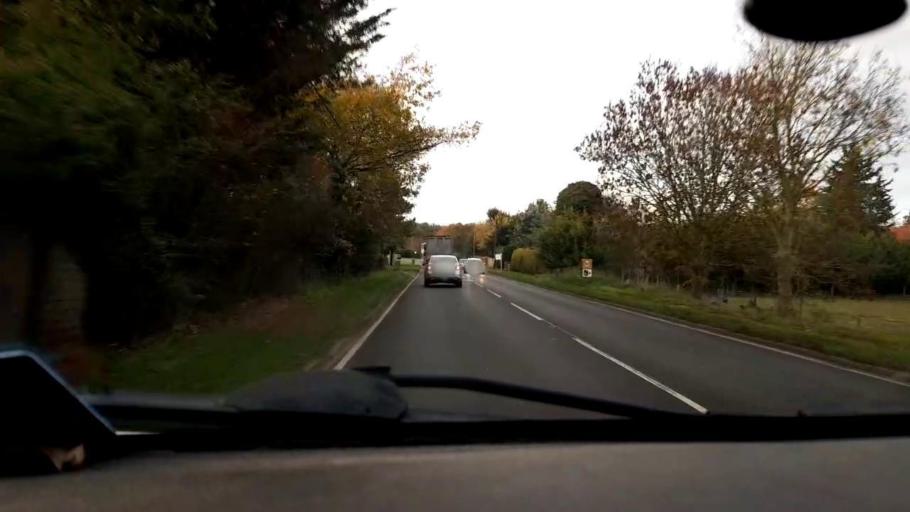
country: GB
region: England
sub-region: Norfolk
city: Costessey
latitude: 52.7099
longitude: 1.1412
